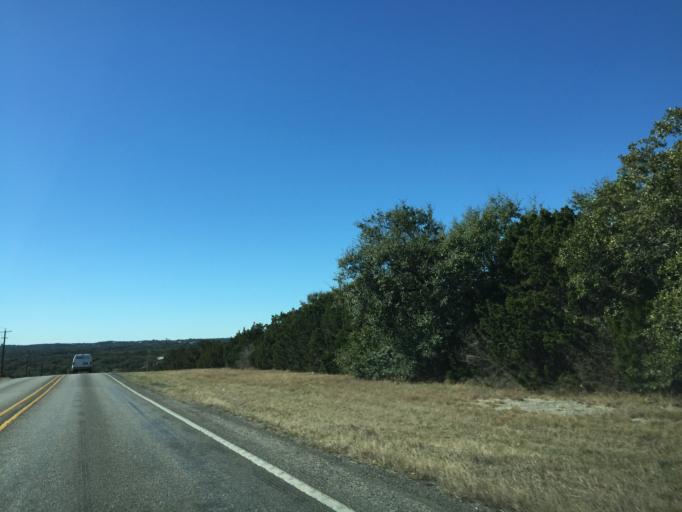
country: US
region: Texas
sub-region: Comal County
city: Garden Ridge
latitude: 29.7078
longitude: -98.3112
